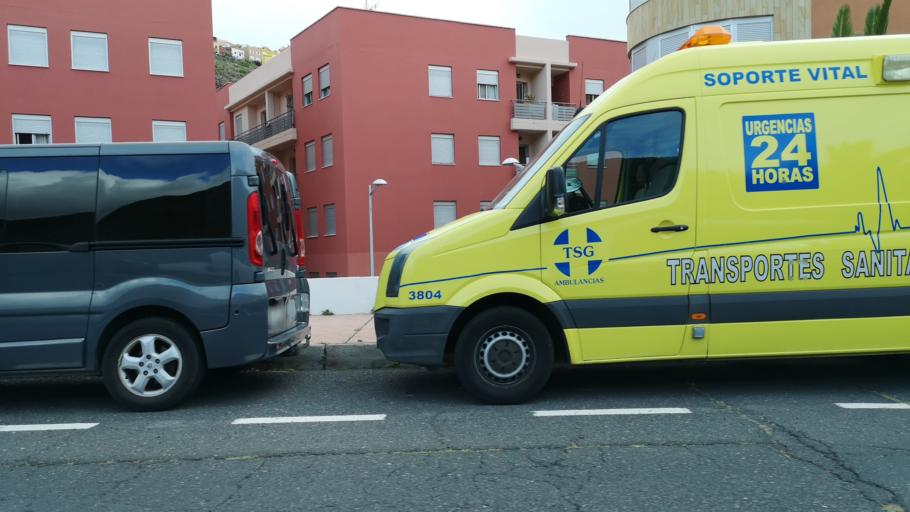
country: ES
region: Canary Islands
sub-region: Provincia de Santa Cruz de Tenerife
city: San Sebastian de la Gomera
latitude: 28.0943
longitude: -17.1148
